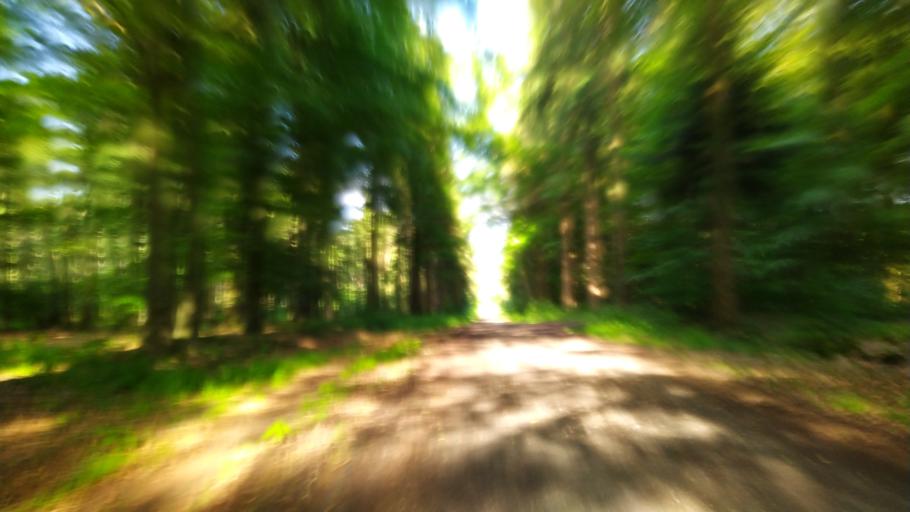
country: DE
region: Lower Saxony
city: Deinstedt
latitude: 53.4390
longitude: 9.2248
